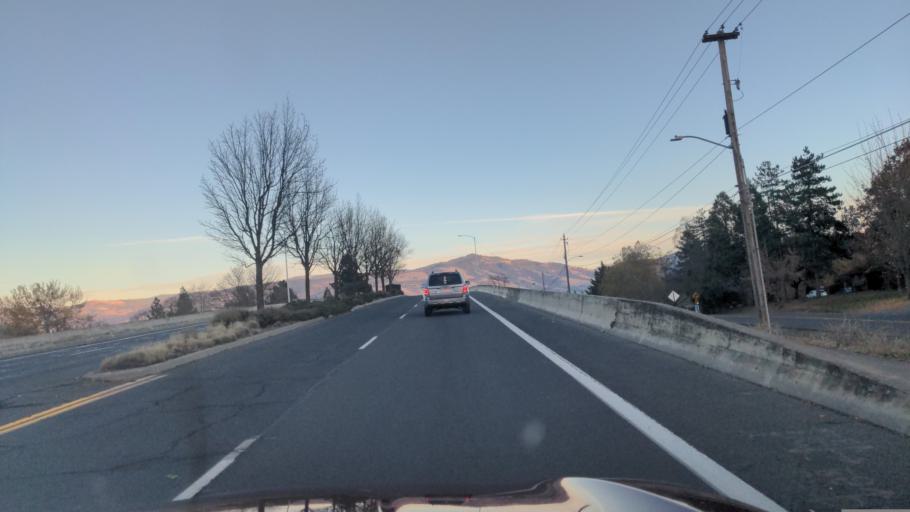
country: US
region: Oregon
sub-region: Jackson County
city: Ashland
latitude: 42.1853
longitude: -122.6791
